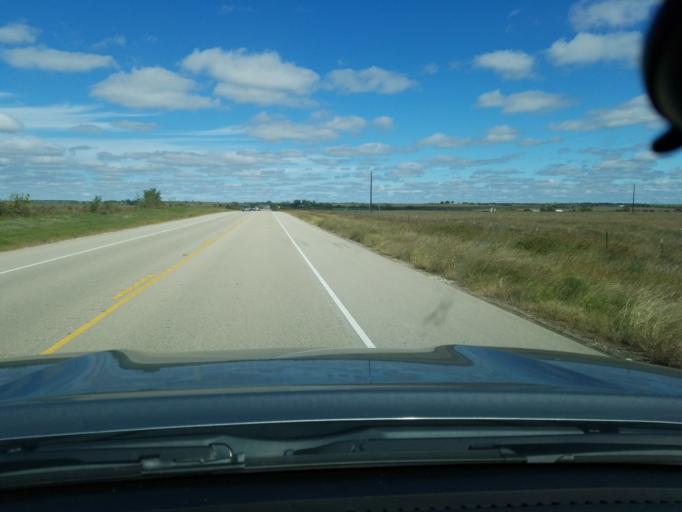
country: US
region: Texas
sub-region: Hamilton County
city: Hamilton
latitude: 31.6342
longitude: -98.1516
